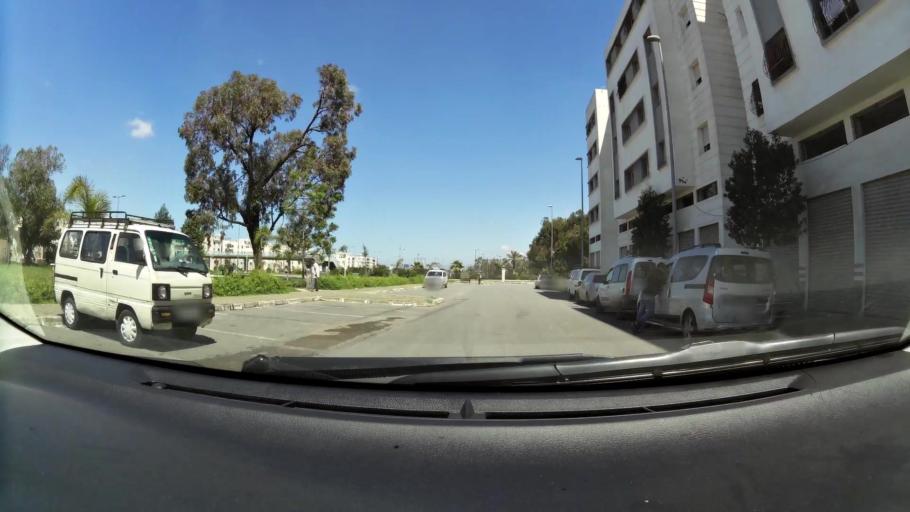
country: MA
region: Grand Casablanca
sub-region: Casablanca
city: Casablanca
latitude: 33.5628
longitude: -7.5823
